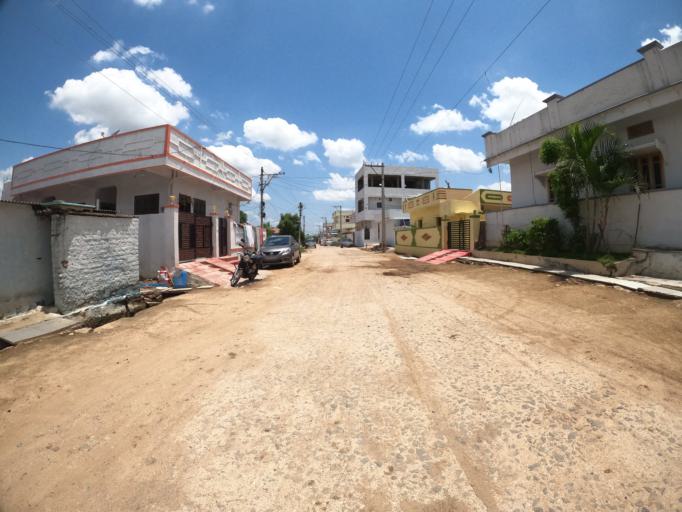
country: IN
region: Telangana
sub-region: Rangareddi
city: Singapur
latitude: 17.4401
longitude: 78.1591
